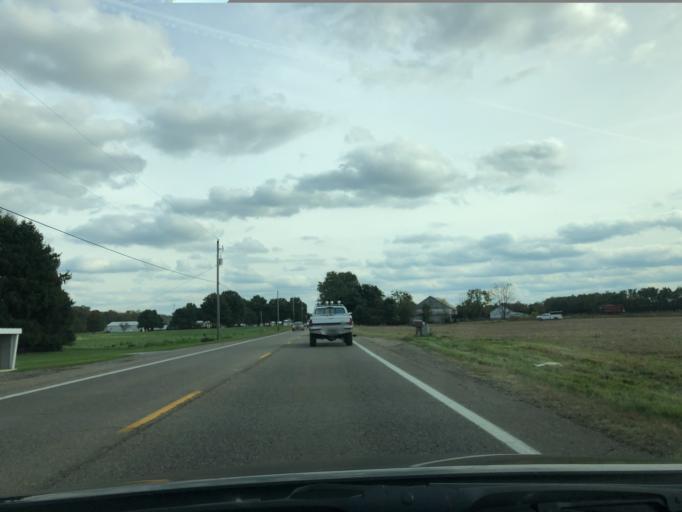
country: US
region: Ohio
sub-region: Tuscarawas County
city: Strasburg
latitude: 40.6219
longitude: -81.5436
